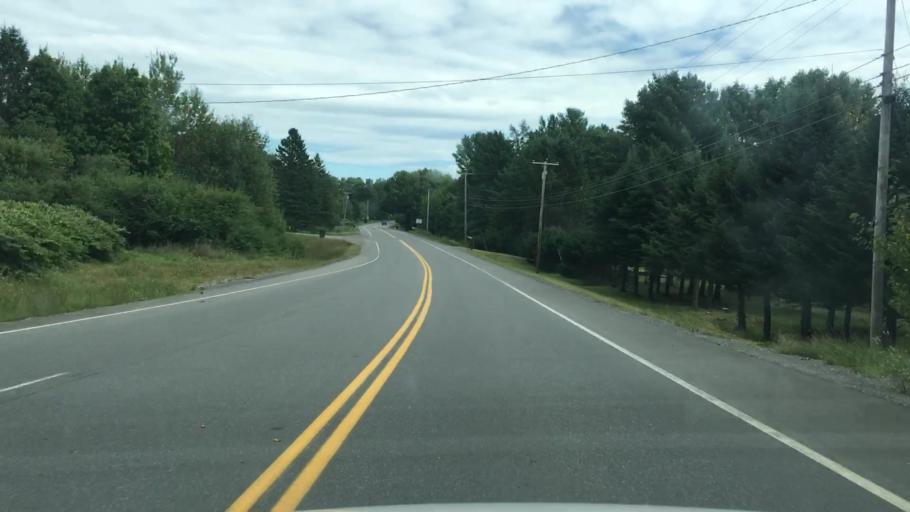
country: US
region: Maine
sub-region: Piscataquis County
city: Milo
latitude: 45.2379
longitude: -69.0507
